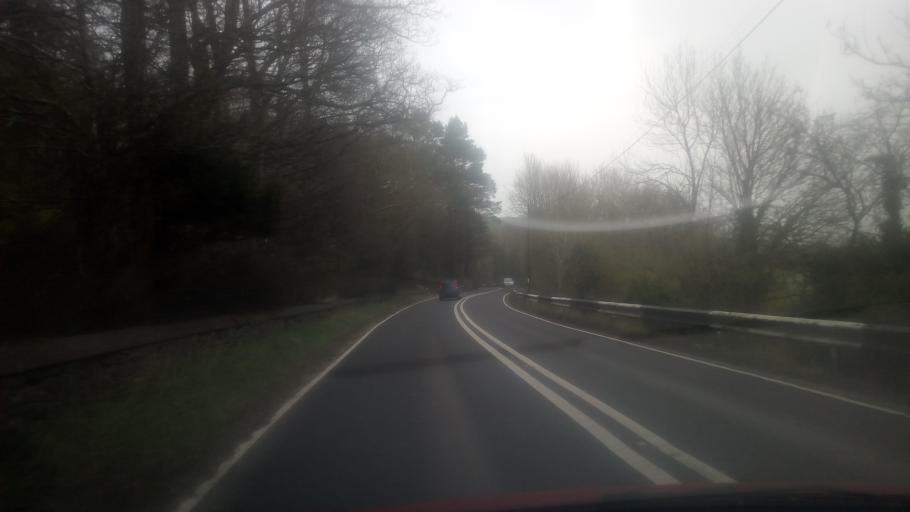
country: GB
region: Scotland
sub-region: The Scottish Borders
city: Galashiels
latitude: 55.6814
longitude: -2.8688
